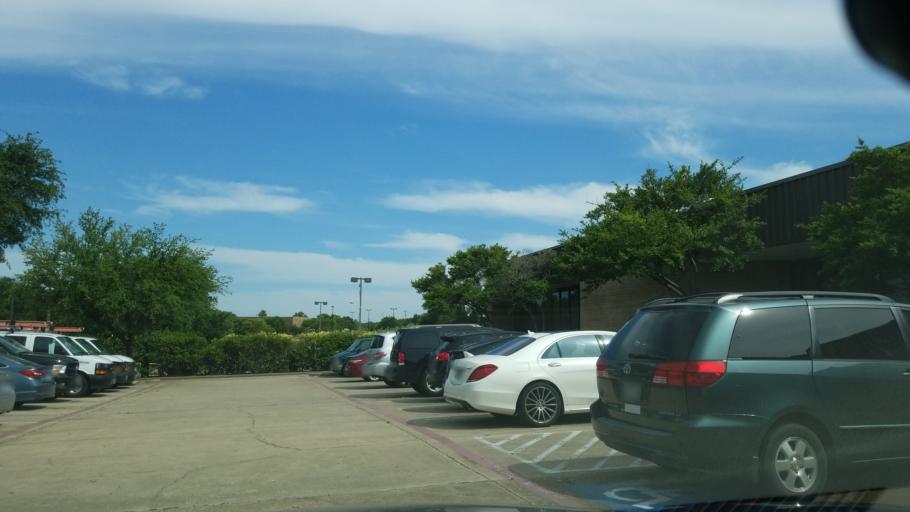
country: US
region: Texas
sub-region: Dallas County
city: Irving
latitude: 32.8828
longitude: -96.9785
